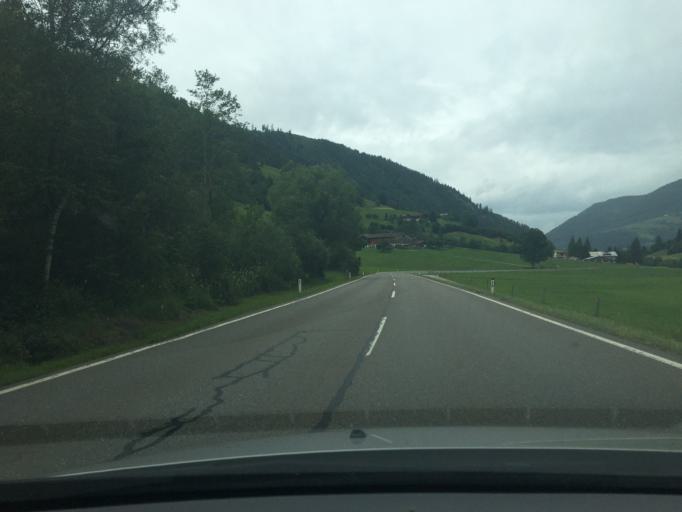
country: AT
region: Salzburg
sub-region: Politischer Bezirk Zell am See
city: Bruck an der Grossglocknerstrasse
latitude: 47.2528
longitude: 12.8244
